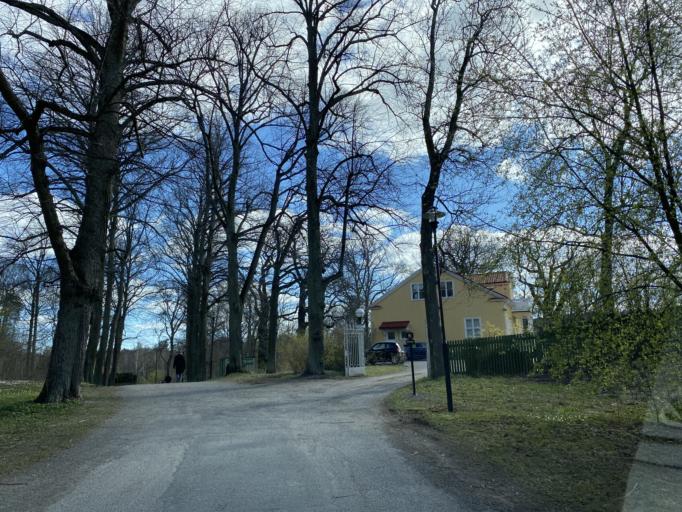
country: SE
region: Stockholm
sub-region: Lidingo
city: Lidingoe
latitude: 59.3325
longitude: 18.1246
